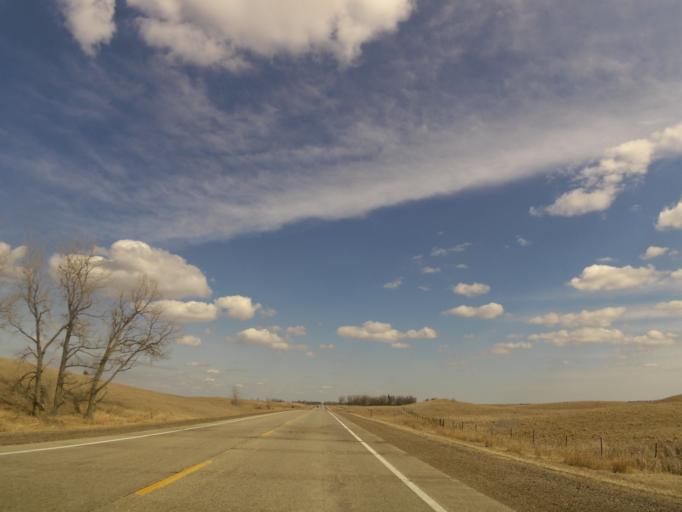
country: US
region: South Dakota
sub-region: Deuel County
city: Clear Lake
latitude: 44.8900
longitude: -96.7159
